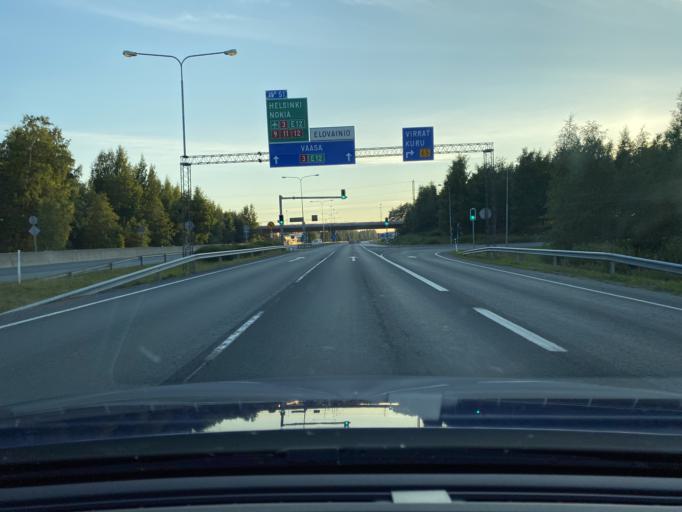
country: FI
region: Pirkanmaa
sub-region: Tampere
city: Yloejaervi
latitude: 61.5542
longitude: 23.5784
